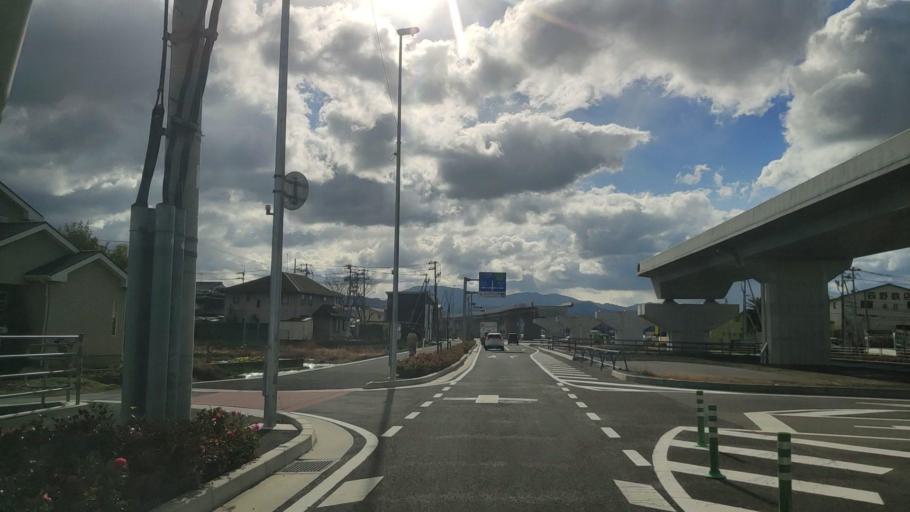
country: JP
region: Ehime
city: Masaki-cho
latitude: 33.8166
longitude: 132.7199
